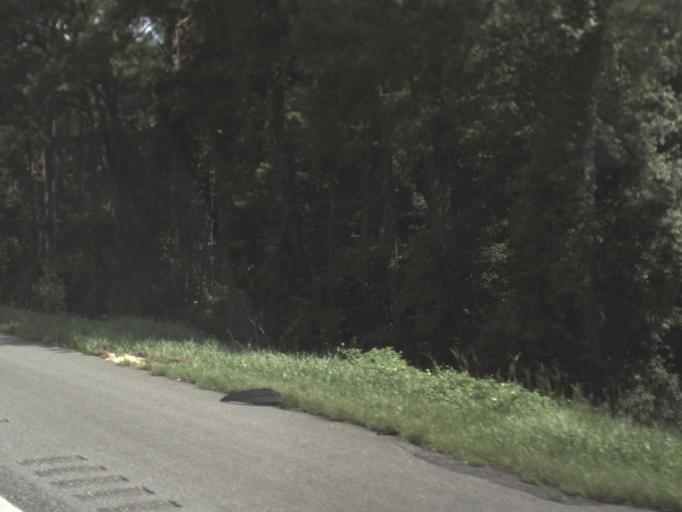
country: US
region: Florida
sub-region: Alachua County
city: High Springs
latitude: 29.9307
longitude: -82.5604
